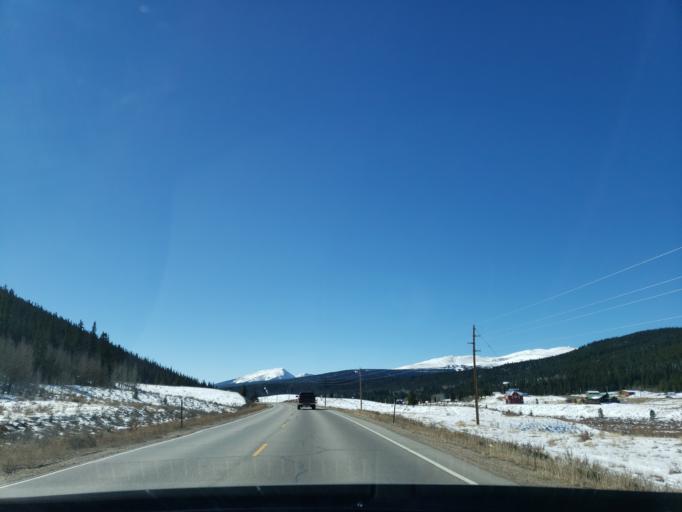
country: US
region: Colorado
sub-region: Park County
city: Fairplay
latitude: 39.3101
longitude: -106.0607
